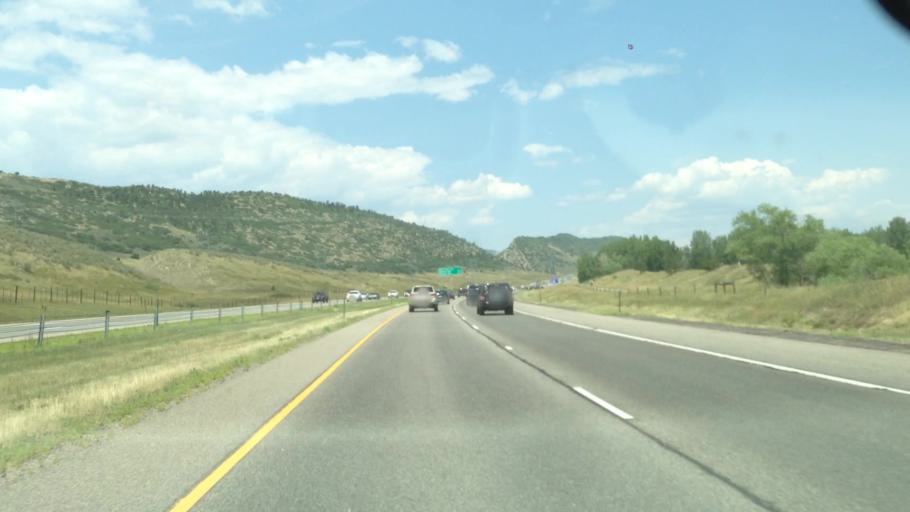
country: US
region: Colorado
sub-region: Jefferson County
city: Ken Caryl
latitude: 39.5638
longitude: -105.1268
